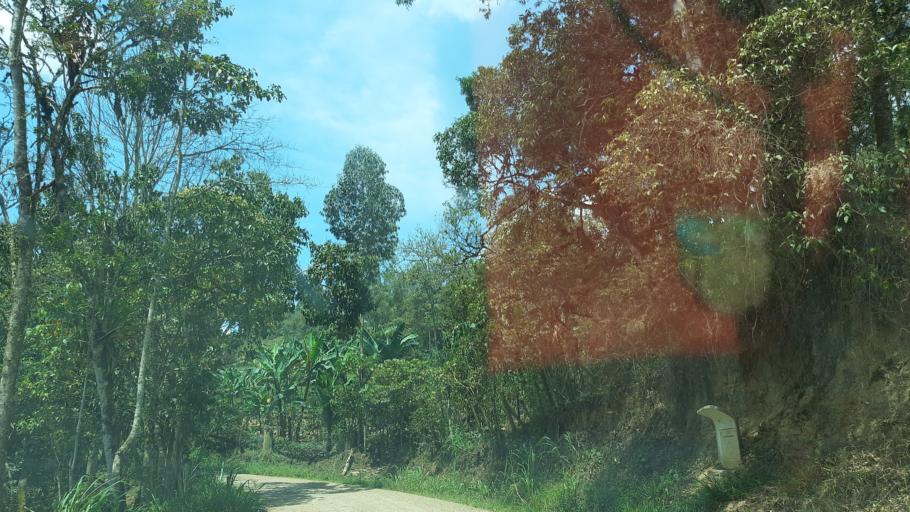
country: CO
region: Boyaca
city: Chinavita
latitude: 5.1287
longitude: -73.3752
